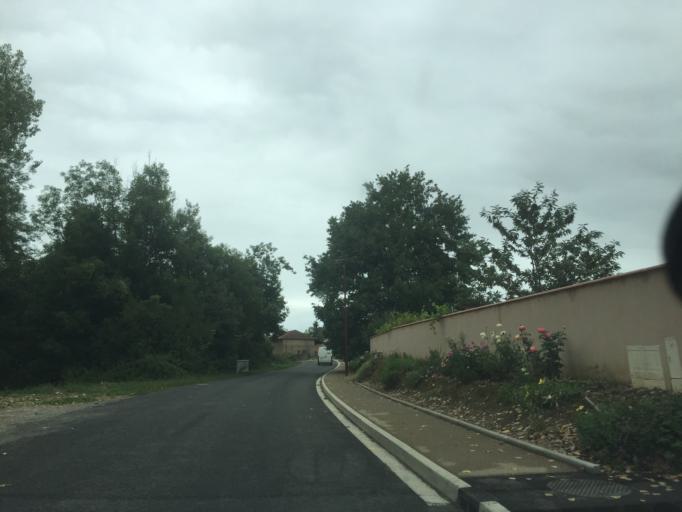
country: FR
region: Midi-Pyrenees
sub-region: Departement des Hautes-Pyrenees
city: Rabastens-de-Bigorre
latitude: 43.3299
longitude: 0.2279
